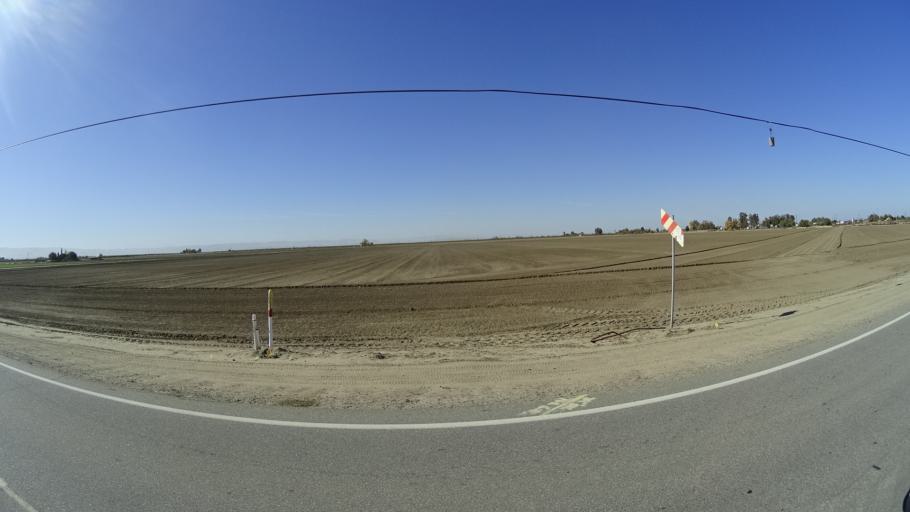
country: US
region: California
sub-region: Kern County
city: Greenfield
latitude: 35.2611
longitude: -119.0743
